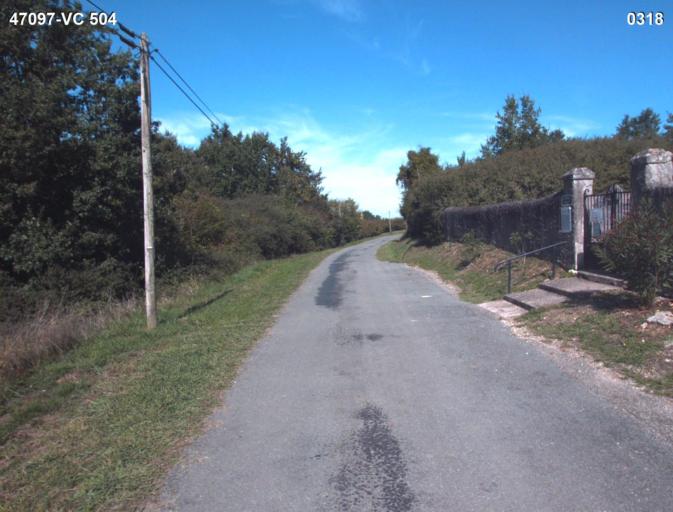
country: FR
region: Aquitaine
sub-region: Departement du Lot-et-Garonne
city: Vianne
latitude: 44.1905
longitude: 0.3515
